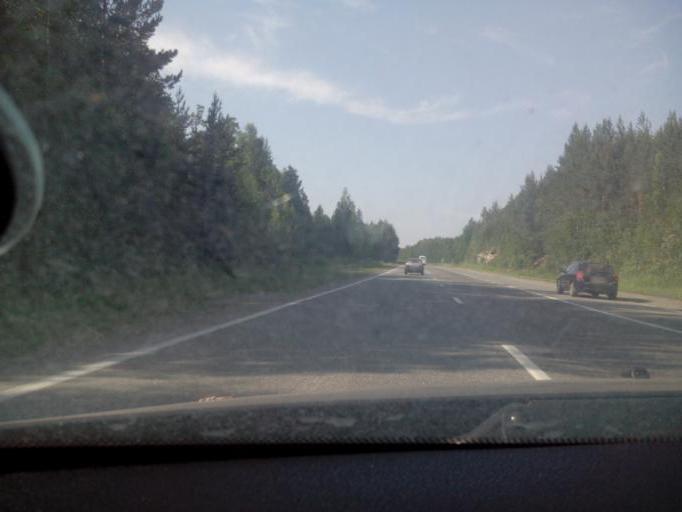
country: RU
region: Sverdlovsk
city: Verkh-Neyvinskiy
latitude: 57.2759
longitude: 60.2959
